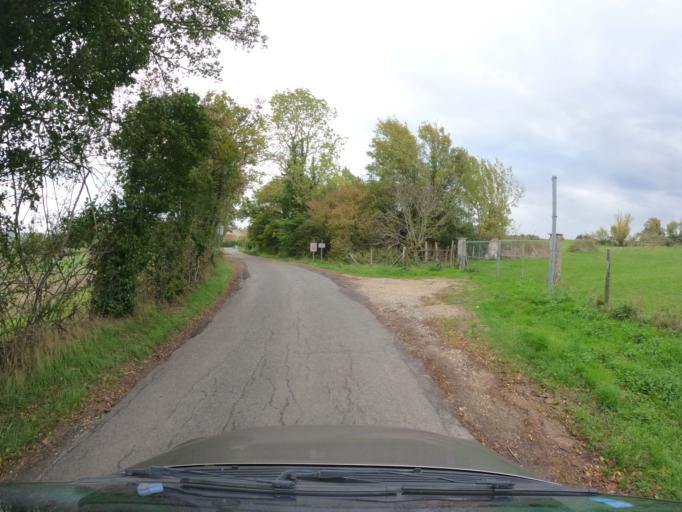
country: FR
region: Ile-de-France
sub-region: Departement de Seine-et-Marne
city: Montry
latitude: 48.8727
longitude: 2.8322
